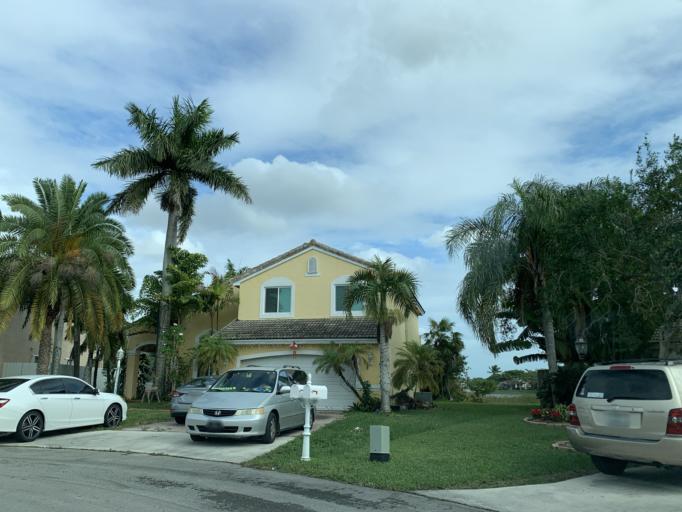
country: US
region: Florida
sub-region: Miami-Dade County
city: Kendall West
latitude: 25.6957
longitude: -80.4537
